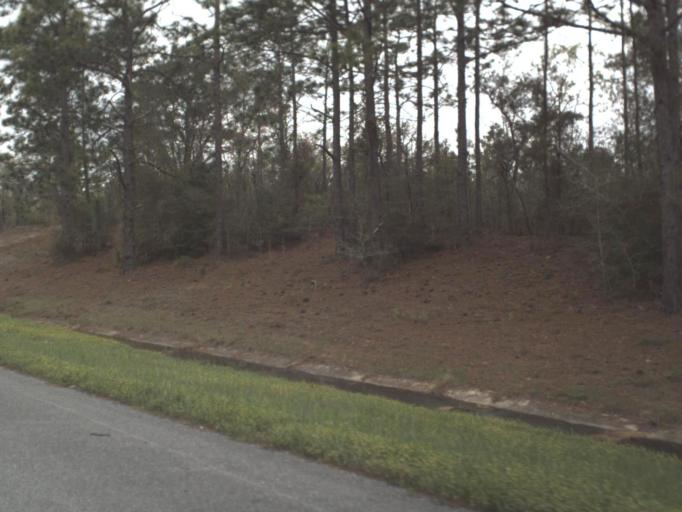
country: US
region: Florida
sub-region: Okaloosa County
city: Crestview
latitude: 30.7270
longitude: -86.5498
